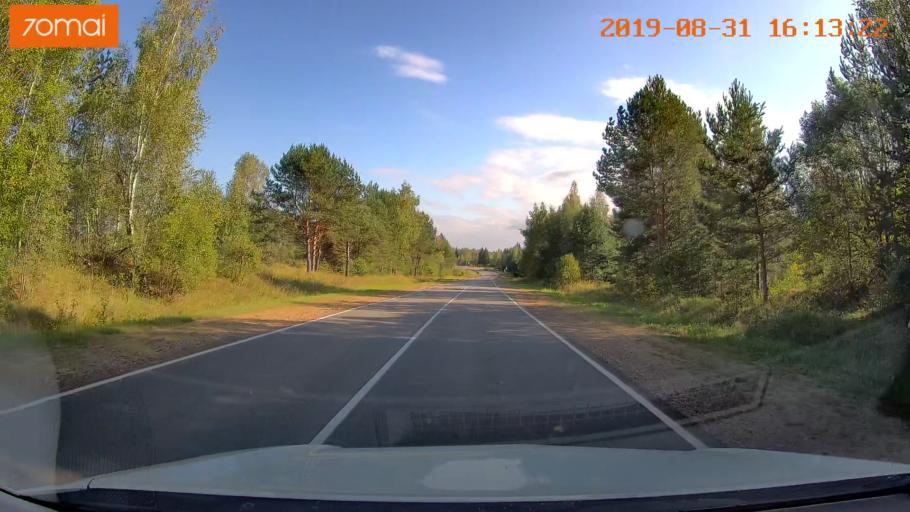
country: RU
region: Kaluga
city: Nikola-Lenivets
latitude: 54.5774
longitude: 35.4449
